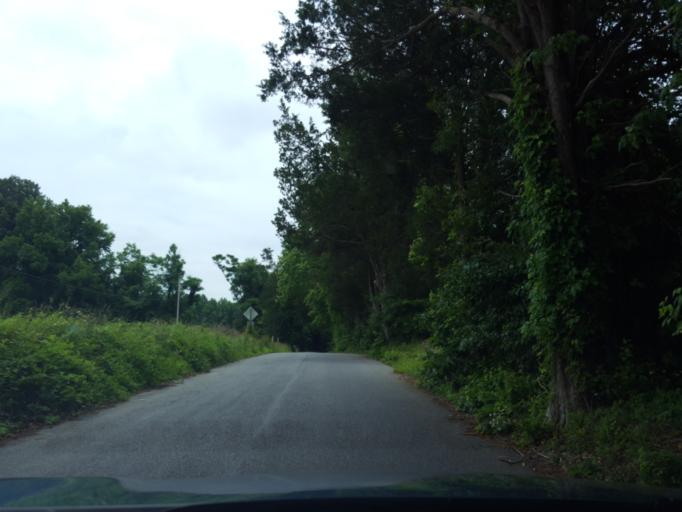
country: US
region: Maryland
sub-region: Prince George's County
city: Marlboro Meadows
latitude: 38.7825
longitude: -76.6846
